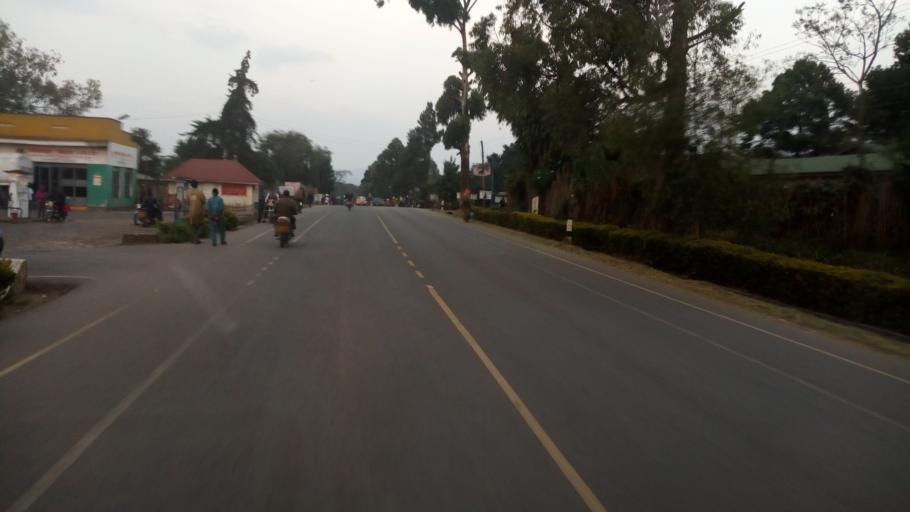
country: UG
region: Western Region
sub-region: Kisoro District
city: Kisoro
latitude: -1.2836
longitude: 29.6875
